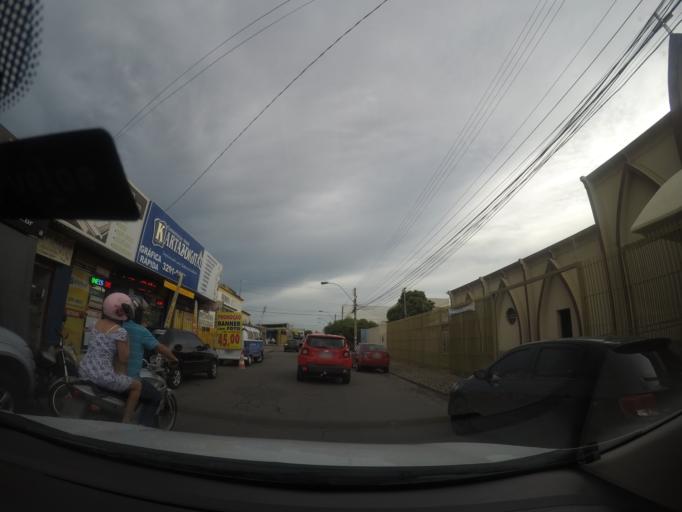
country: BR
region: Goias
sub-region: Goiania
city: Goiania
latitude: -16.6743
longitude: -49.2917
